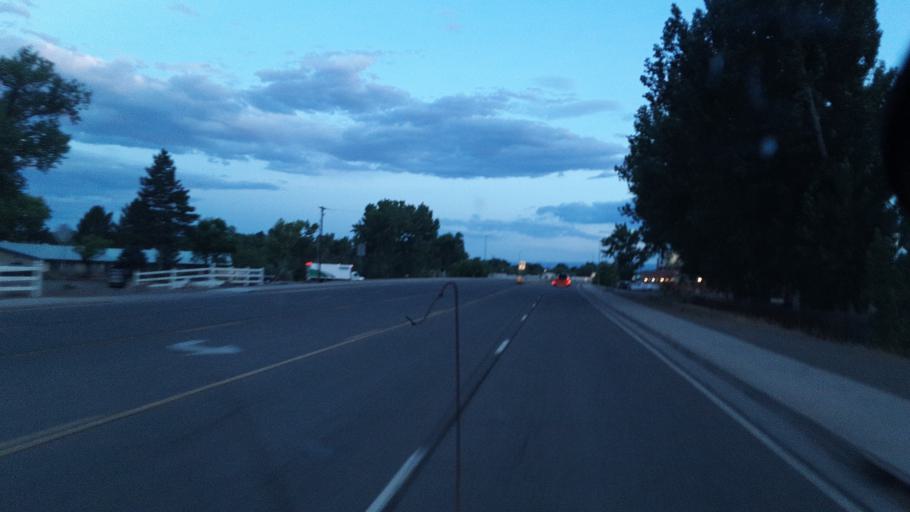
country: US
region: Colorado
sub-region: Delta County
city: Delta
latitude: 38.7530
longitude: -108.0694
